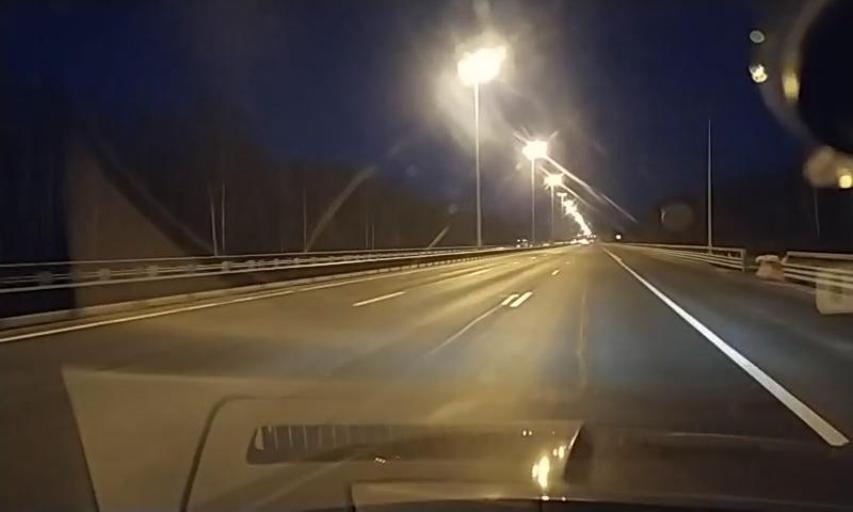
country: RU
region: St.-Petersburg
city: Pesochnyy
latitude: 60.0957
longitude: 30.0947
